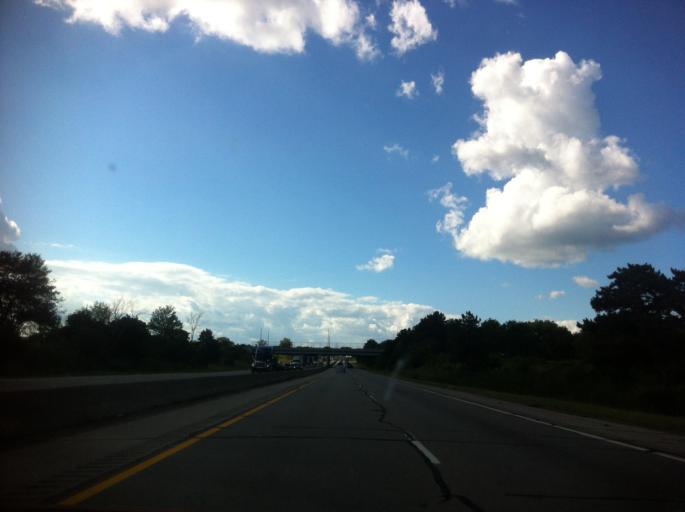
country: US
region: Michigan
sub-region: Washtenaw County
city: Ann Arbor
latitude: 42.2373
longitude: -83.7499
